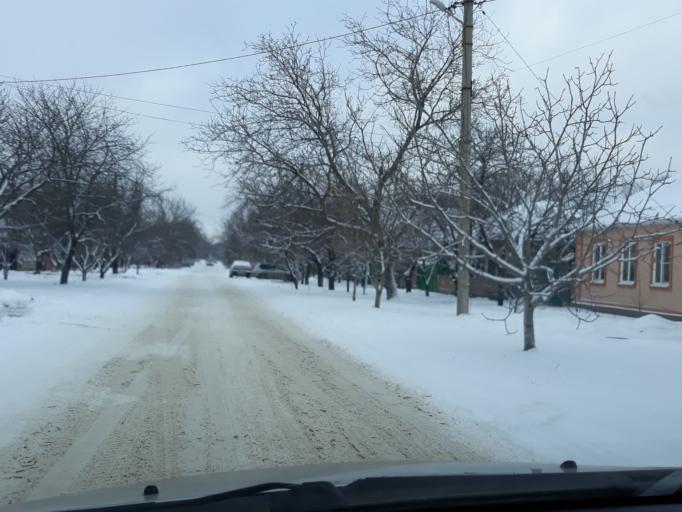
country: RU
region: Rostov
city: Taganrog
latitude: 47.2293
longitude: 38.8831
